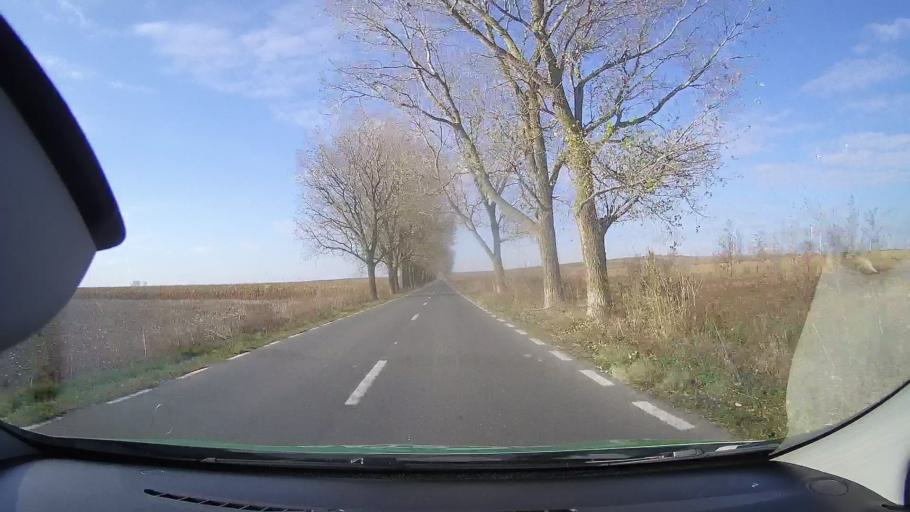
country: RO
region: Tulcea
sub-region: Comuna Valea Nucarilor
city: Iazurile
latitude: 45.0264
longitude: 29.0013
